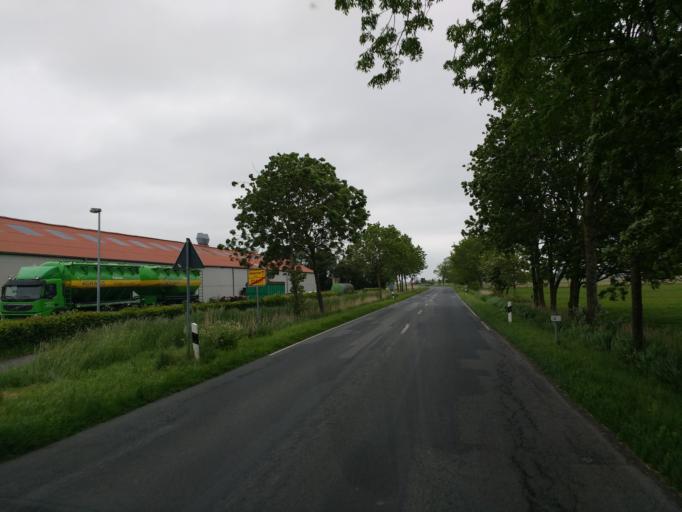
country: DE
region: Lower Saxony
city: Jever
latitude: 53.6365
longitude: 7.9243
